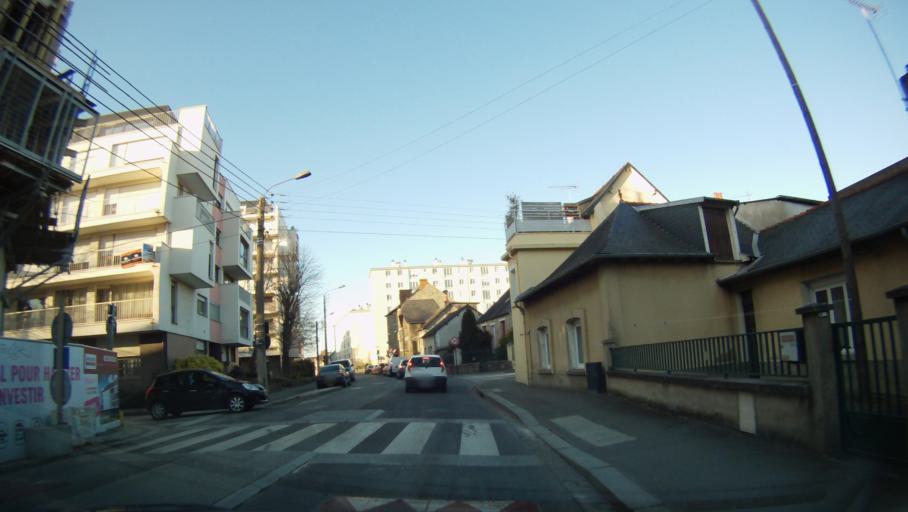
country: FR
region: Brittany
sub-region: Departement d'Ille-et-Vilaine
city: Rennes
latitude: 48.0927
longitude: -1.6712
